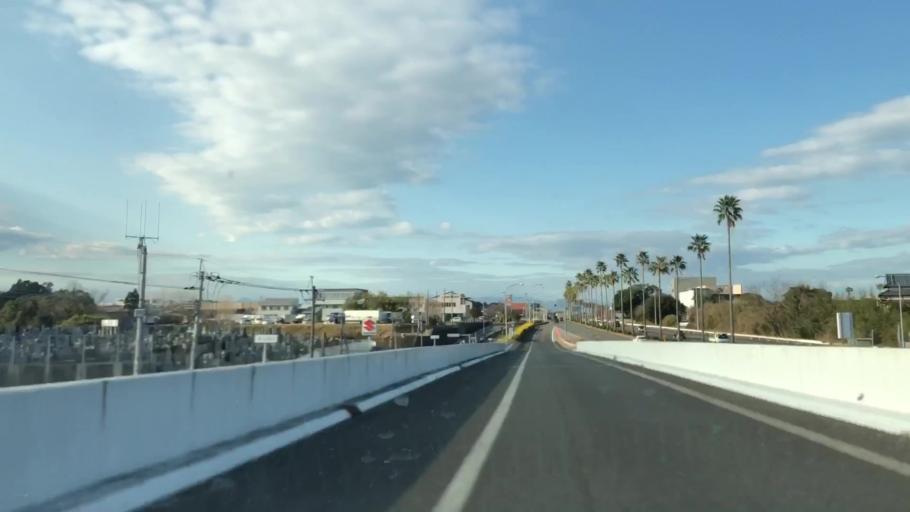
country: JP
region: Miyazaki
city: Miyazaki-shi
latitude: 31.8717
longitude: 131.4143
